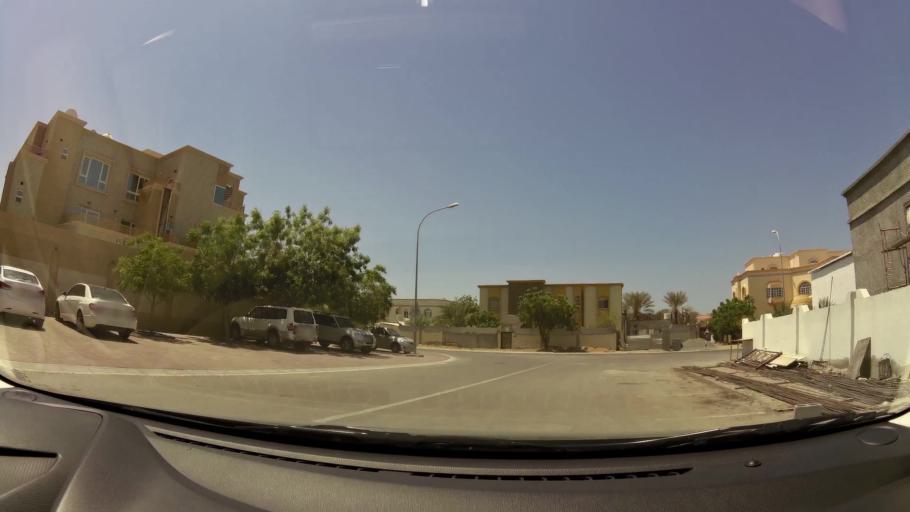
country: OM
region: Muhafazat Masqat
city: As Sib al Jadidah
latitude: 23.6145
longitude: 58.2288
